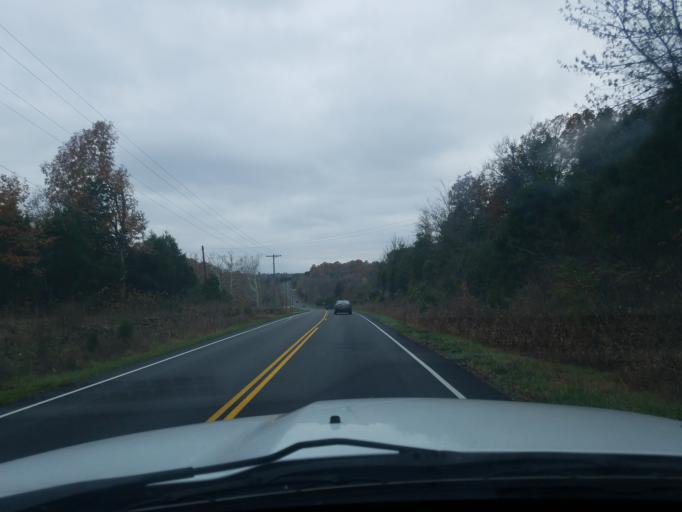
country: US
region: Kentucky
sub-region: Nelson County
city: Bardstown
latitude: 37.7871
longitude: -85.4082
